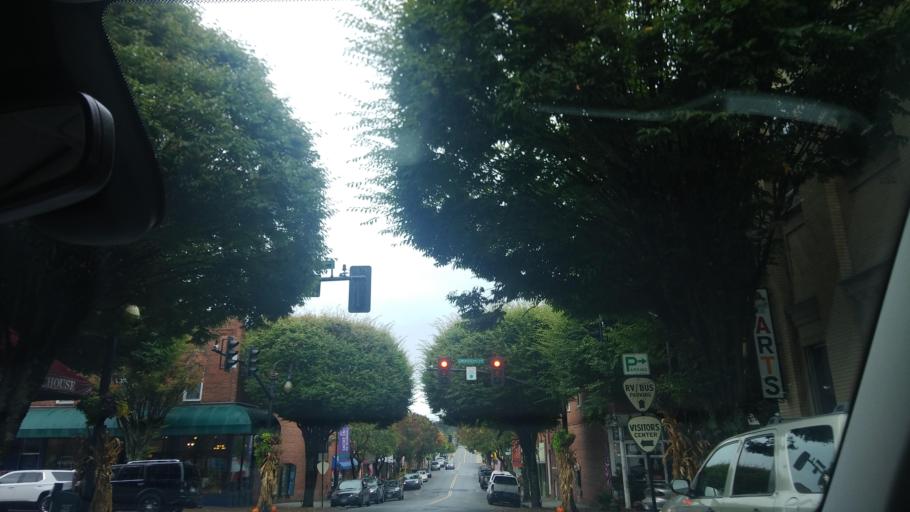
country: US
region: Virginia
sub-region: City of Galax
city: Galax
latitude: 36.6621
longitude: -80.9249
